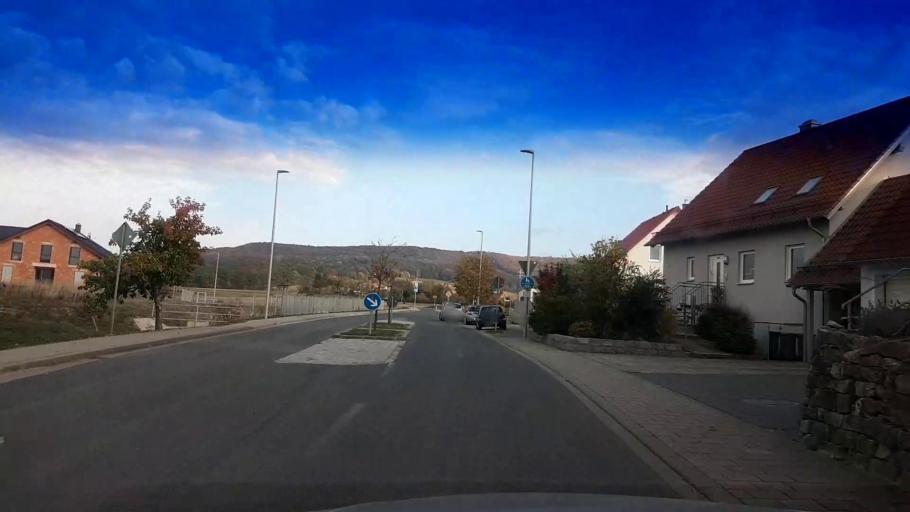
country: DE
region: Bavaria
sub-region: Upper Franconia
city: Schesslitz
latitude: 49.9737
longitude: 11.0471
